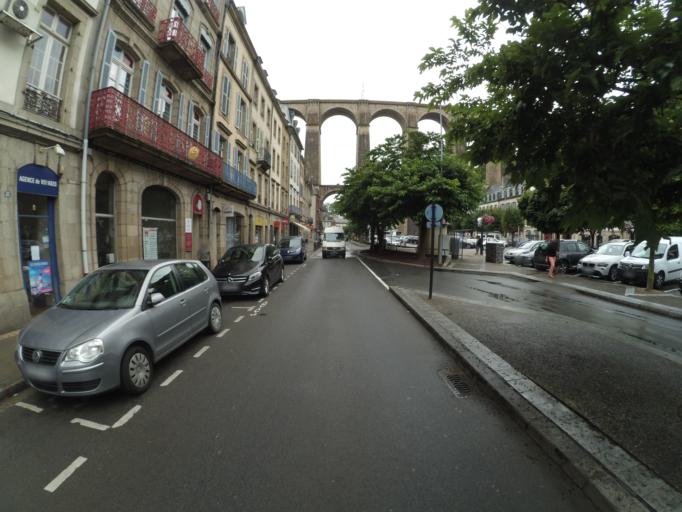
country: FR
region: Brittany
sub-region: Departement du Finistere
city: Morlaix
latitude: 48.5801
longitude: -3.8299
